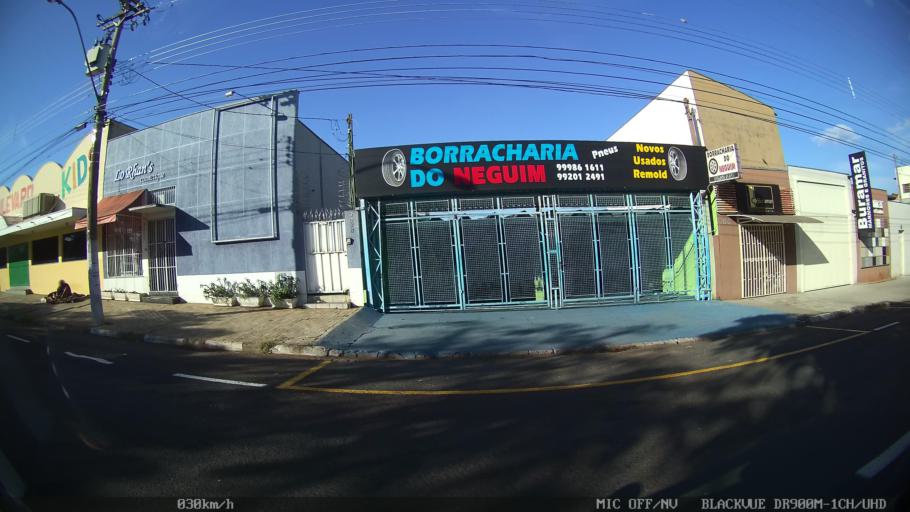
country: BR
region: Sao Paulo
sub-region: Franca
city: Franca
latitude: -20.5156
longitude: -47.3980
